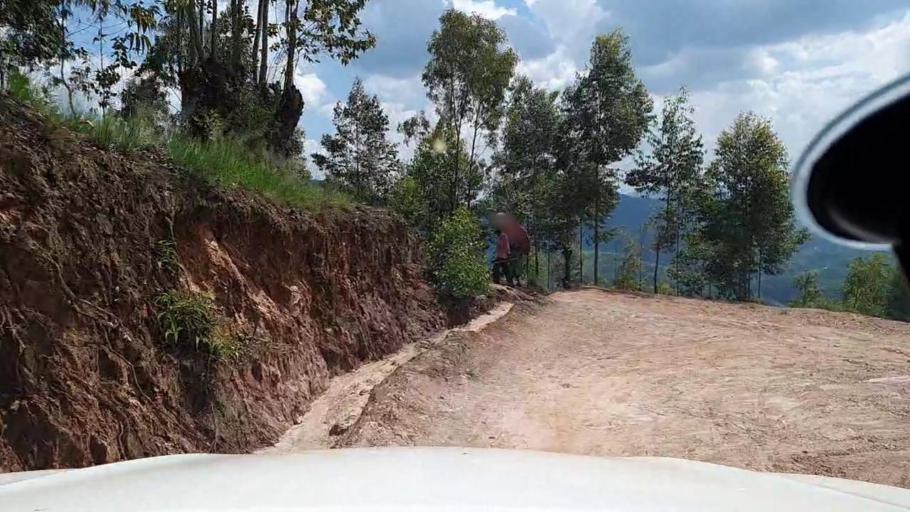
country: RW
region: Southern Province
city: Gitarama
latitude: -1.8409
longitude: 29.8207
